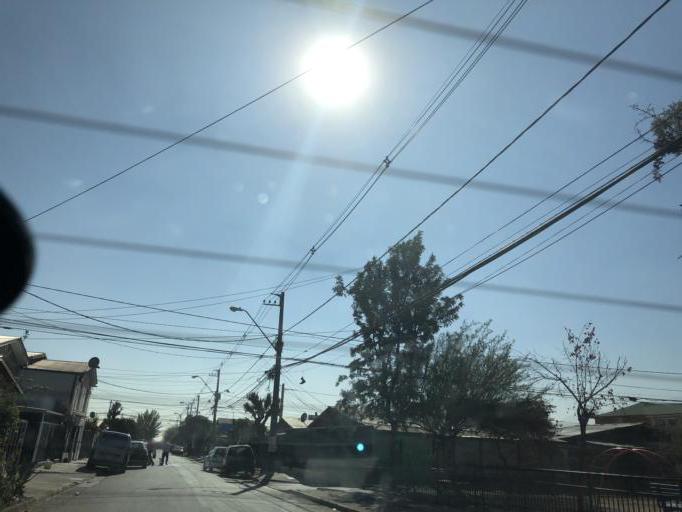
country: CL
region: Santiago Metropolitan
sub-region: Provincia de Cordillera
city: Puente Alto
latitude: -33.6073
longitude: -70.5961
